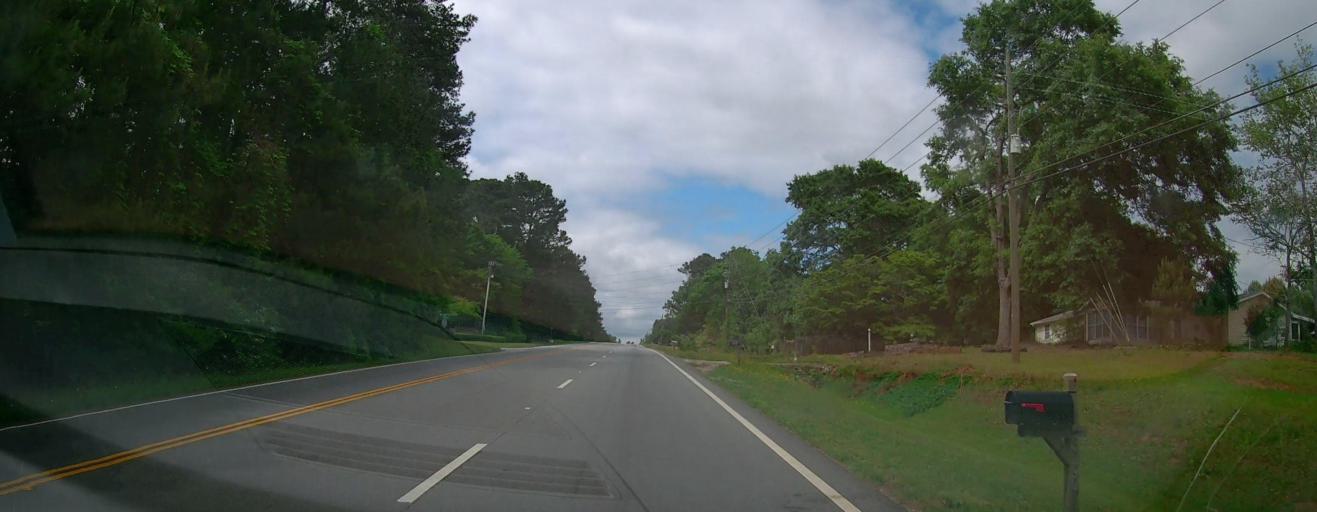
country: US
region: Georgia
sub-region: DeKalb County
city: Pine Mountain
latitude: 33.6072
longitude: -84.0952
